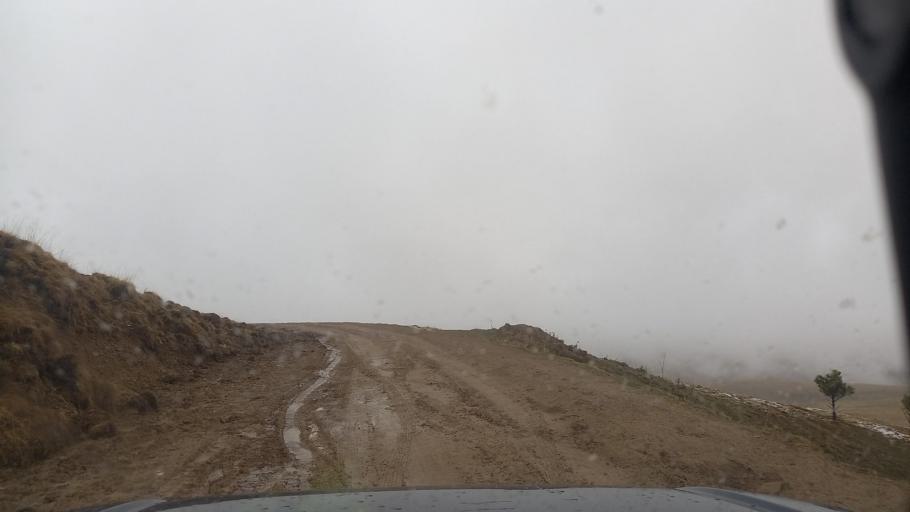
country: RU
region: Karachayevo-Cherkesiya
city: Uchkeken
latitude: 43.6082
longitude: 42.5682
